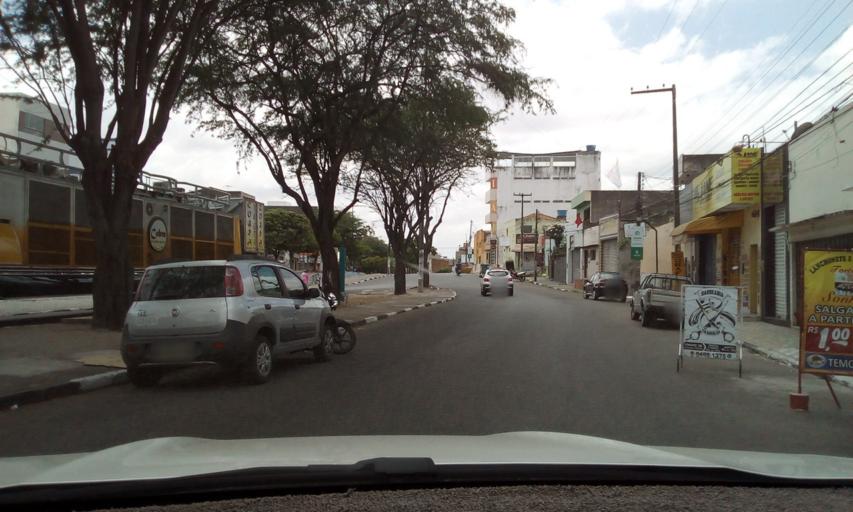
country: BR
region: Pernambuco
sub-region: Caruaru
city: Caruaru
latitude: -8.2791
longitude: -35.9748
